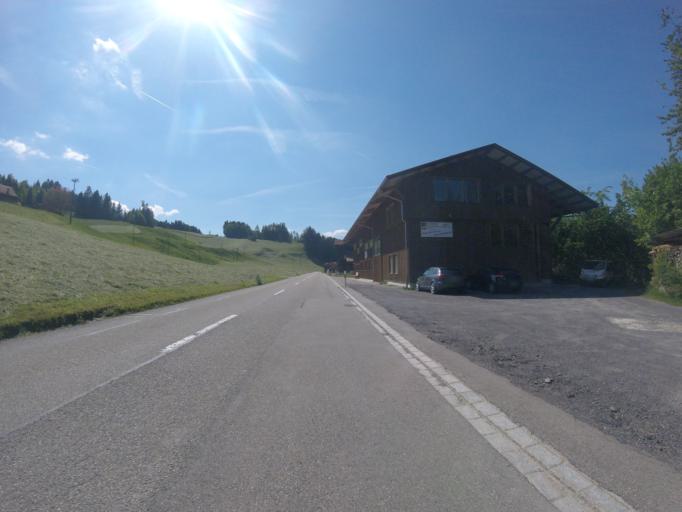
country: CH
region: Saint Gallen
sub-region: Wahlkreis Toggenburg
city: Mogelsberg
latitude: 47.3766
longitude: 9.1209
